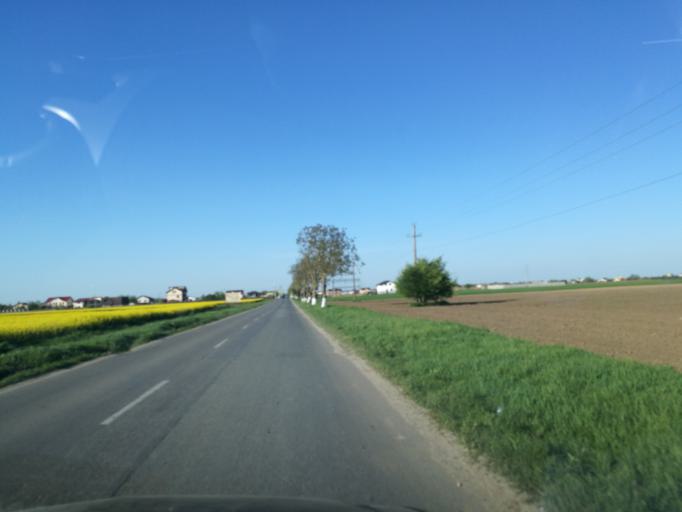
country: RO
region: Ilfov
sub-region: Comuna Berceni
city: Berceni
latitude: 44.2861
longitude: 26.1829
